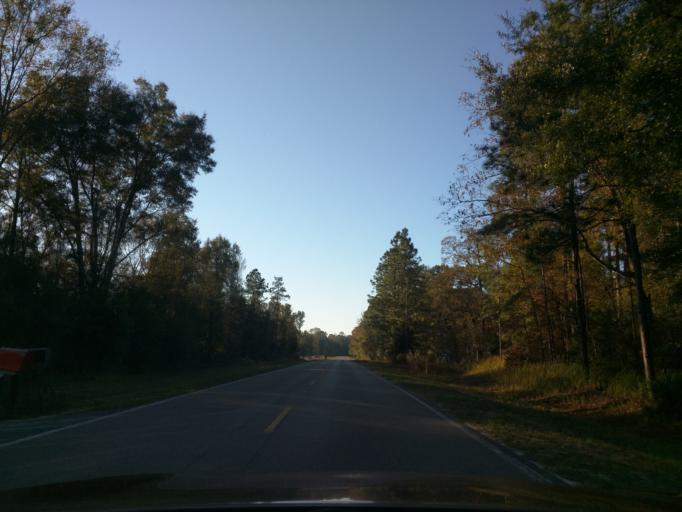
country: US
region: Florida
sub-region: Leon County
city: Woodville
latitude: 30.2947
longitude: -84.1585
